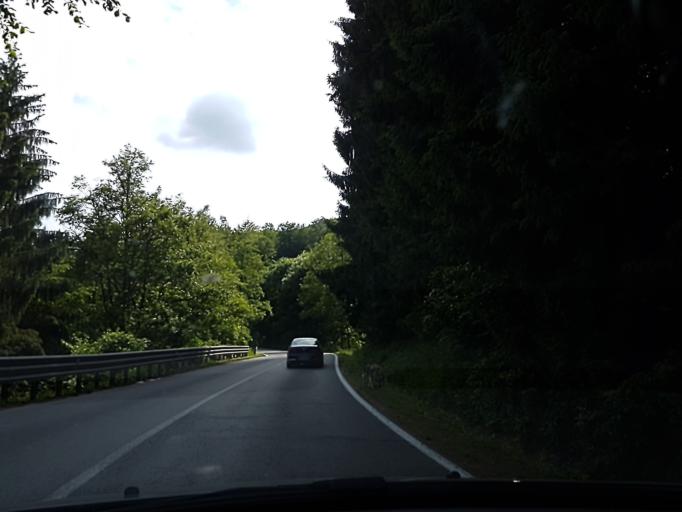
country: RO
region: Prahova
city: Maneciu
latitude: 45.3568
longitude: 25.9431
